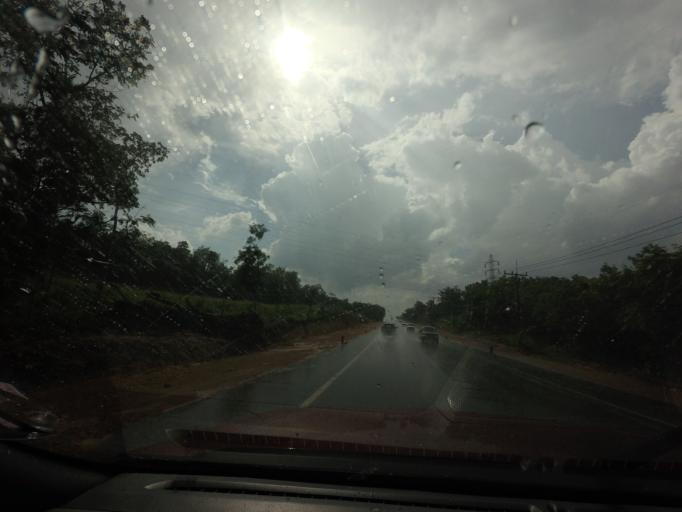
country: TH
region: Yala
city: Krong Pi Nang
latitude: 6.3929
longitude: 101.2882
